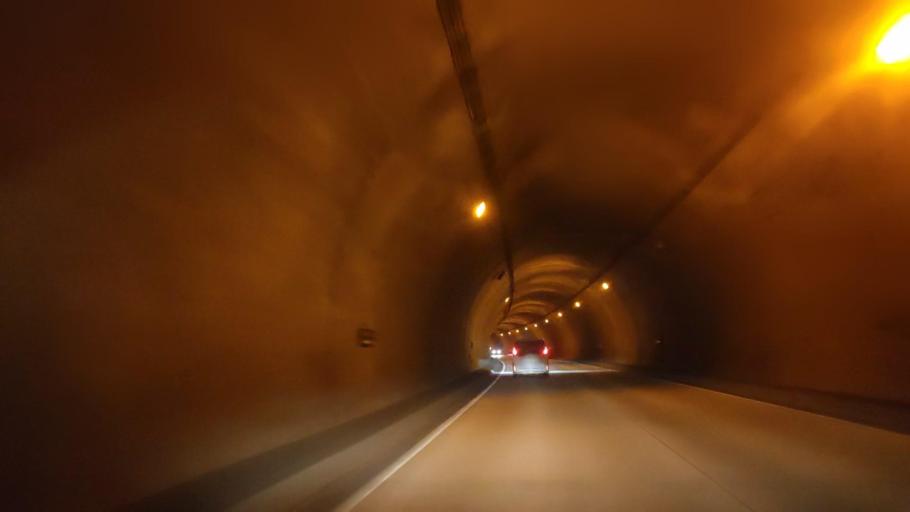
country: JP
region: Hokkaido
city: Shimo-furano
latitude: 43.3414
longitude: 142.2669
